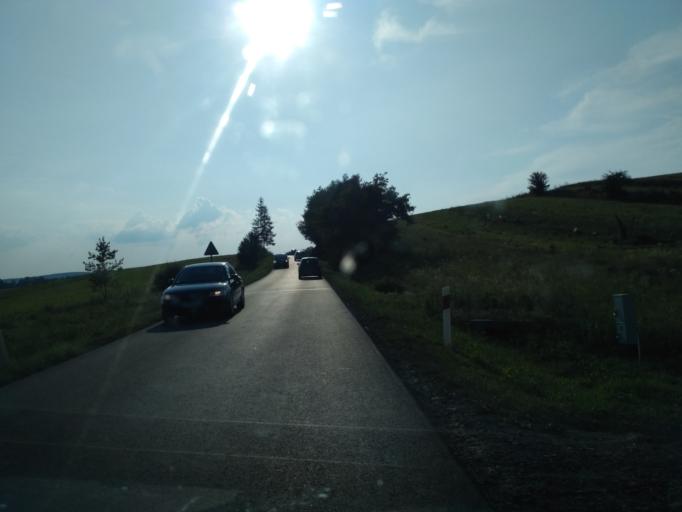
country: PL
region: Subcarpathian Voivodeship
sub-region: Powiat sanocki
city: Sanok
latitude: 49.5866
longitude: 22.1780
